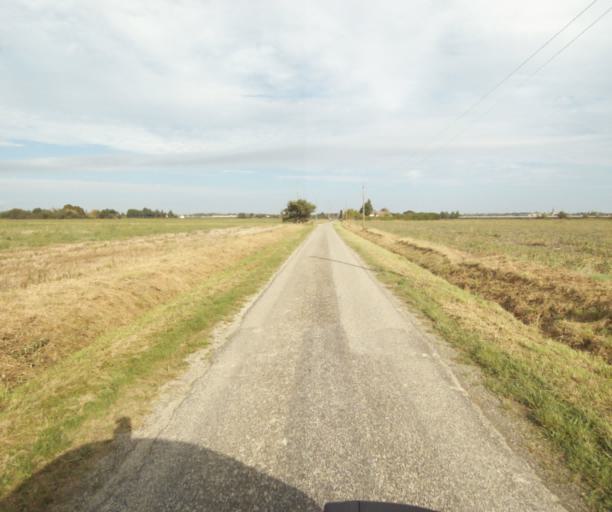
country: FR
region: Midi-Pyrenees
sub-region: Departement du Tarn-et-Garonne
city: Montech
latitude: 43.9369
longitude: 1.2233
